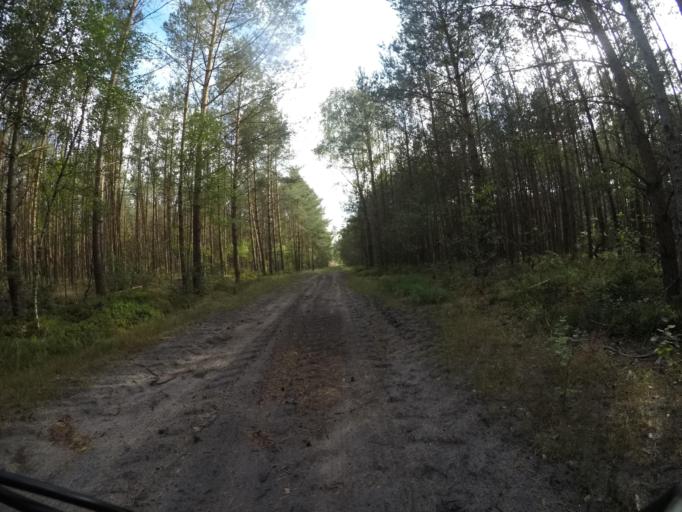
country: DE
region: Lower Saxony
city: Neu Darchau
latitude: 53.2736
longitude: 10.9655
